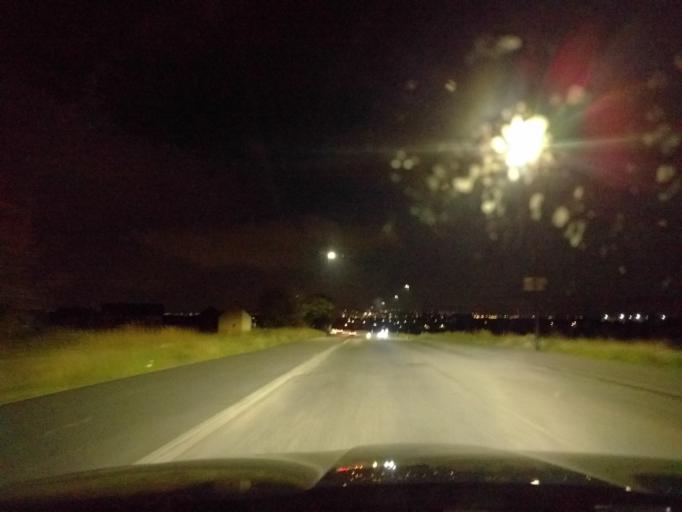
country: GB
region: England
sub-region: Borough of North Tyneside
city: Wallsend
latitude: 55.0142
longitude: -1.5485
